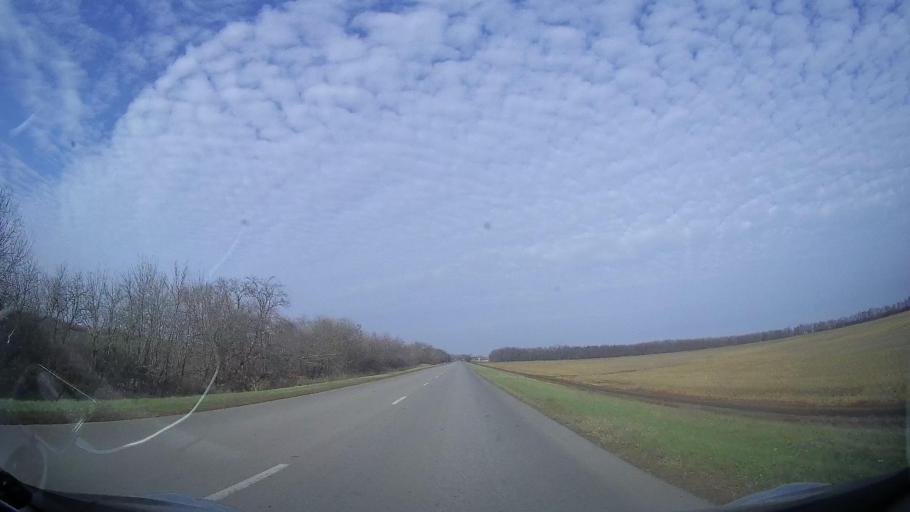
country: RU
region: Rostov
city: Gigant
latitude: 46.8284
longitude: 41.3374
